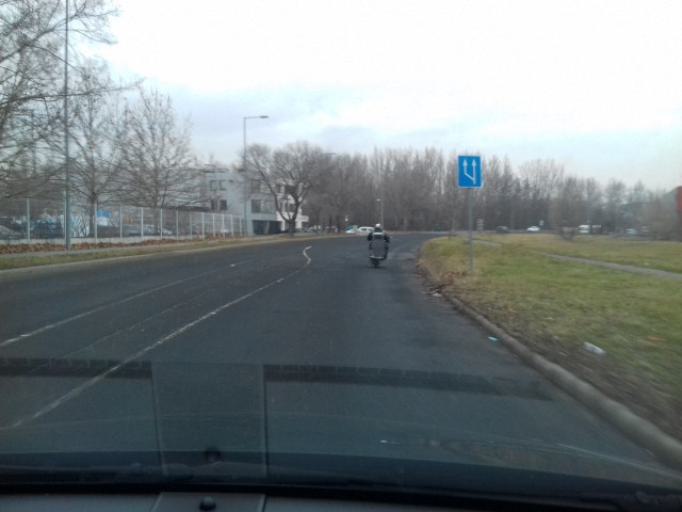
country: HU
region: Budapest
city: Budapest XV. keruelet
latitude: 47.5951
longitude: 19.1058
